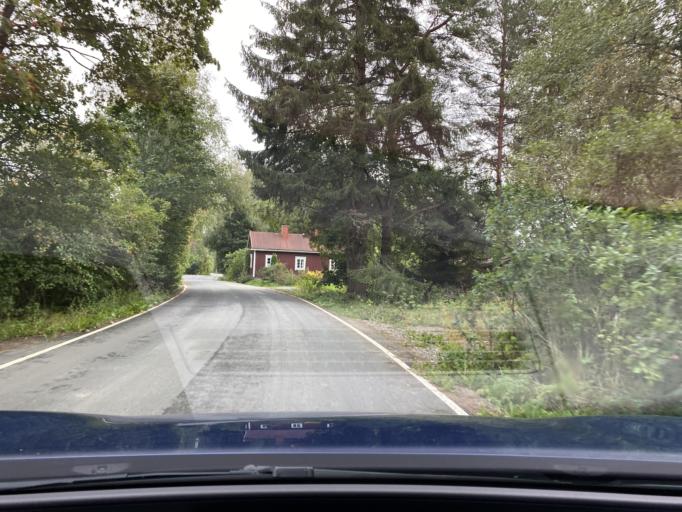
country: FI
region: Pirkanmaa
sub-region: Lounais-Pirkanmaa
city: Punkalaidun
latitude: 61.1676
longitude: 23.1800
